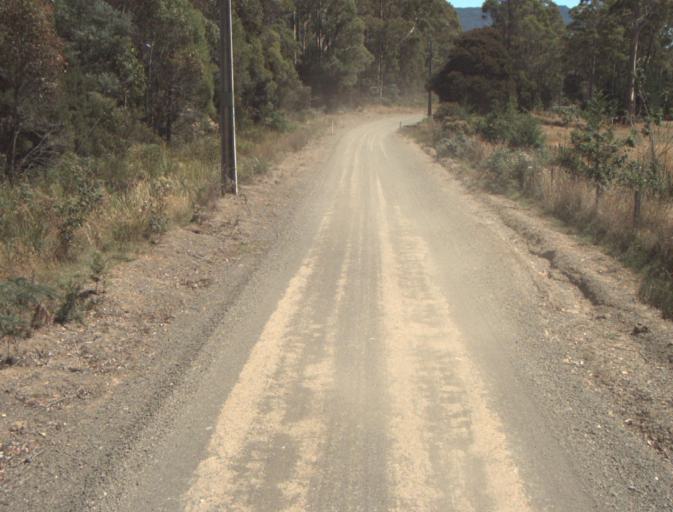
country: AU
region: Tasmania
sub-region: Launceston
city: Newstead
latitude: -41.3445
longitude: 147.3699
